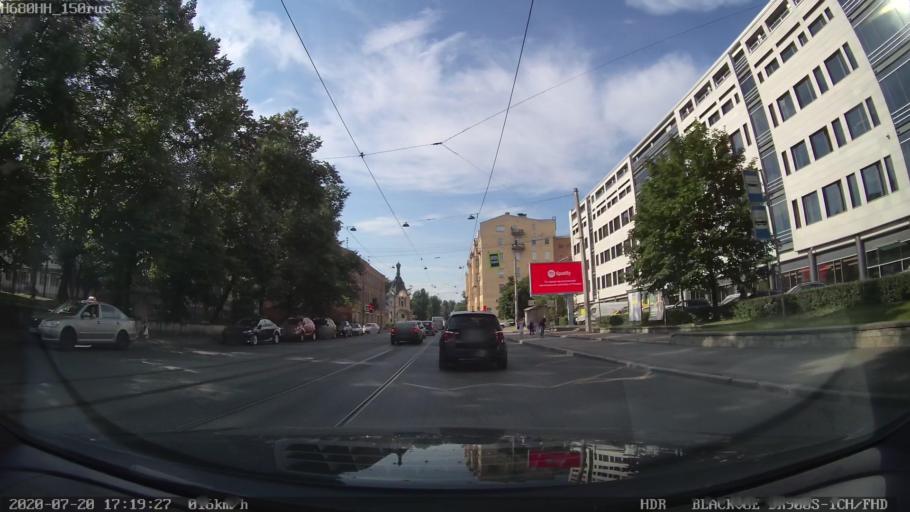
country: RU
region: St.-Petersburg
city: Admiralteisky
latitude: 59.9049
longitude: 30.2772
